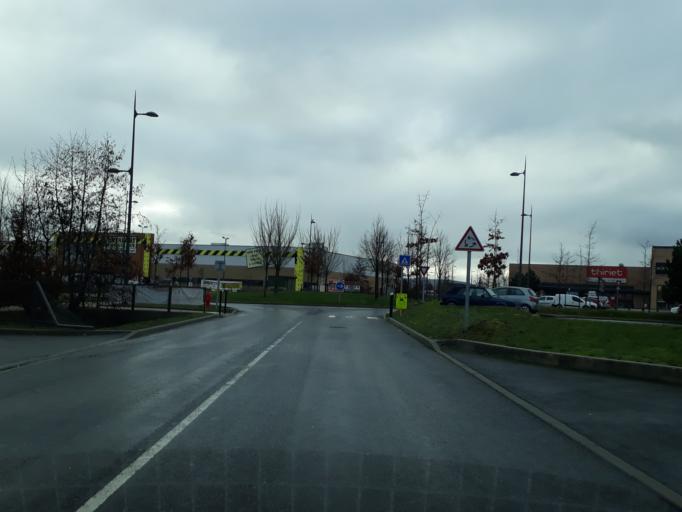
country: FR
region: Ile-de-France
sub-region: Departement de l'Essonne
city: Mennecy
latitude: 48.5661
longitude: 2.4506
